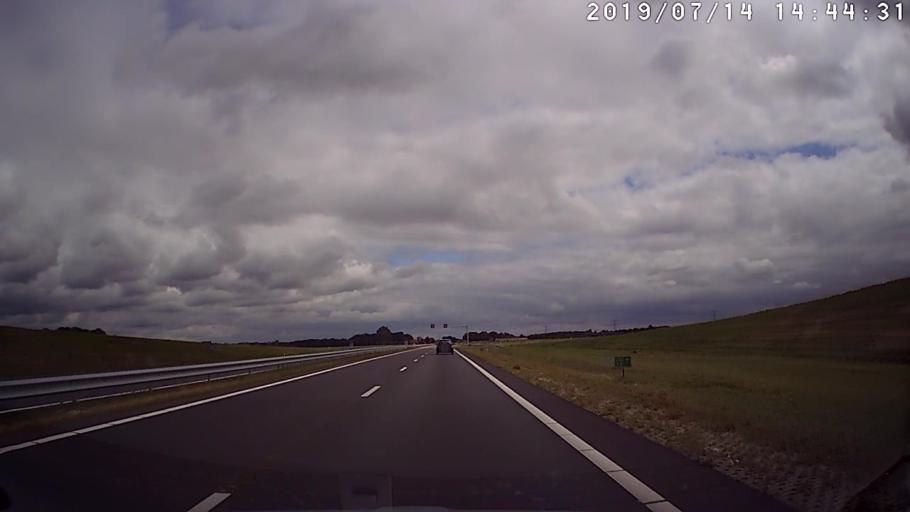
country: NL
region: Overijssel
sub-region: Gemeente Raalte
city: Heino
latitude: 52.4832
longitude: 6.1776
